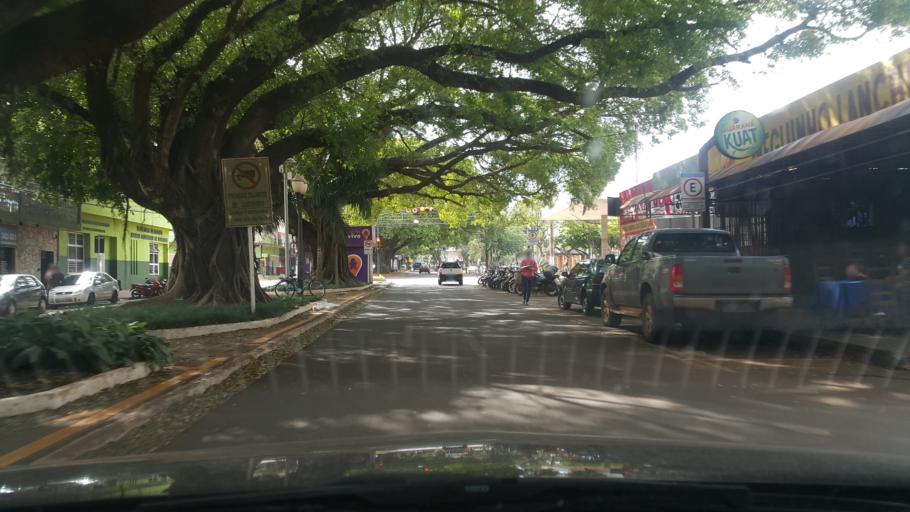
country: BR
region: Mato Grosso do Sul
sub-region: Dourados
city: Dourados
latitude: -22.2299
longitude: -54.8116
